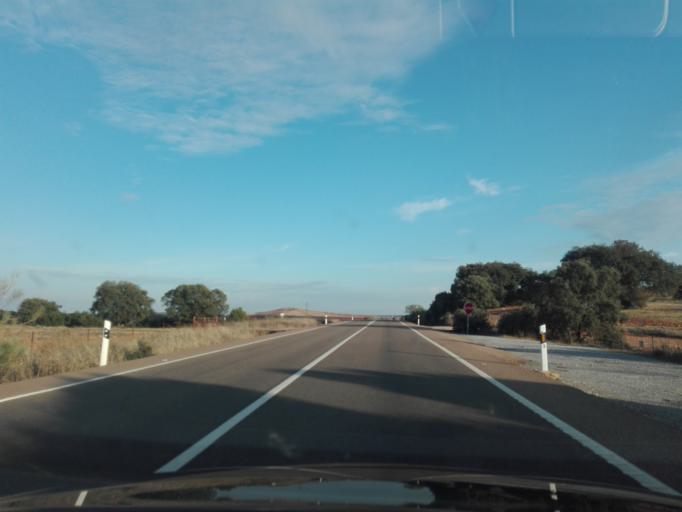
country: ES
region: Extremadura
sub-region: Provincia de Badajoz
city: Usagre
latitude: 38.3649
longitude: -6.2315
